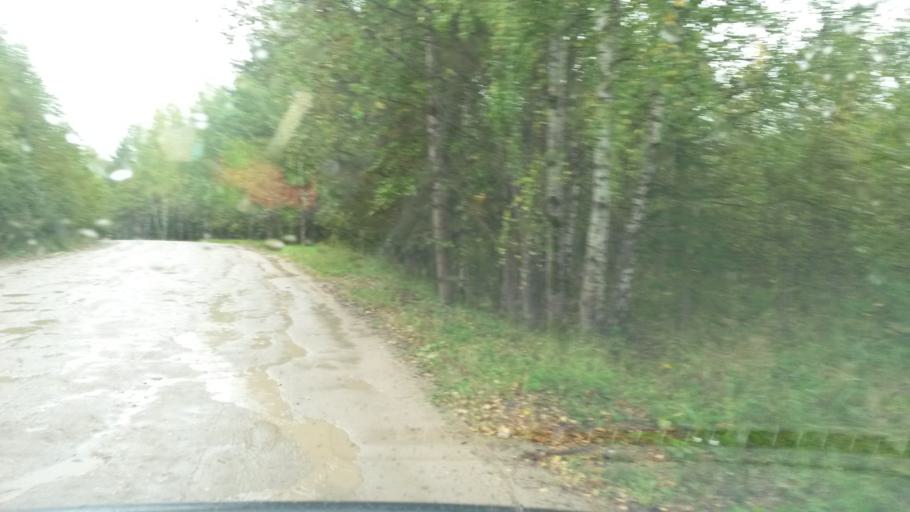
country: RU
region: Ivanovo
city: Zarechnyy
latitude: 57.5033
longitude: 42.2882
